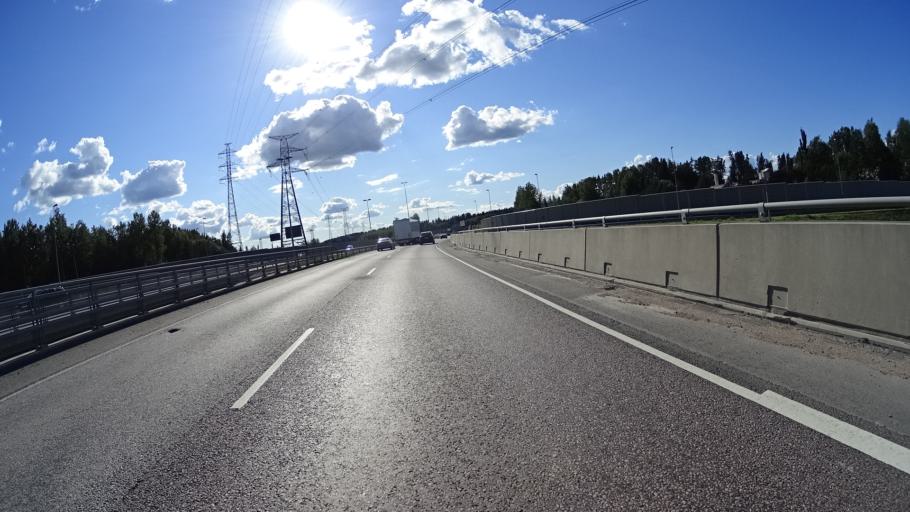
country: FI
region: Uusimaa
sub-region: Helsinki
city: Teekkarikylae
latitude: 60.2925
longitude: 24.8555
